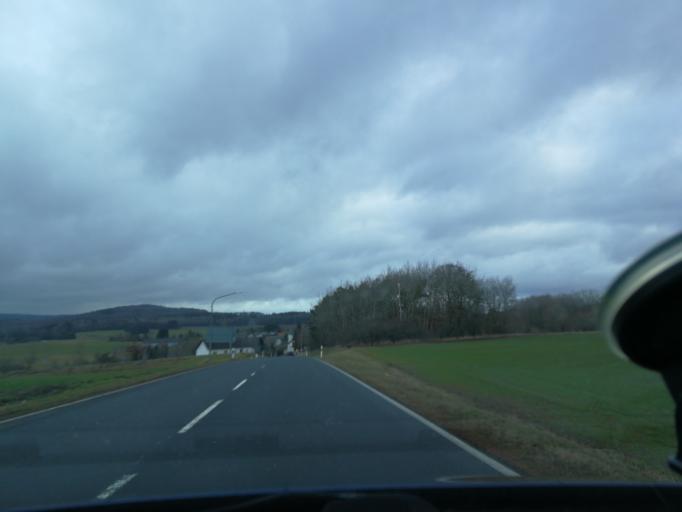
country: DE
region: Rheinland-Pfalz
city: Oberehe-Stroheich
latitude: 50.2807
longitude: 6.7536
